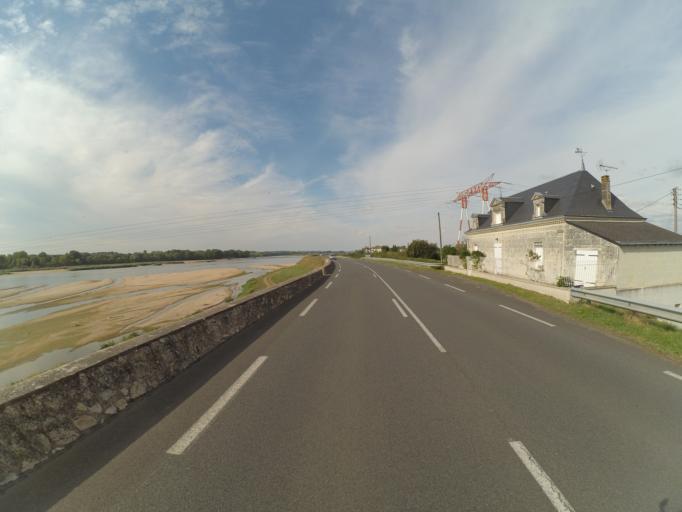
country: FR
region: Pays de la Loire
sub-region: Departement de Maine-et-Loire
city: Varennes-sur-Loire
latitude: 47.2295
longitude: 0.0443
